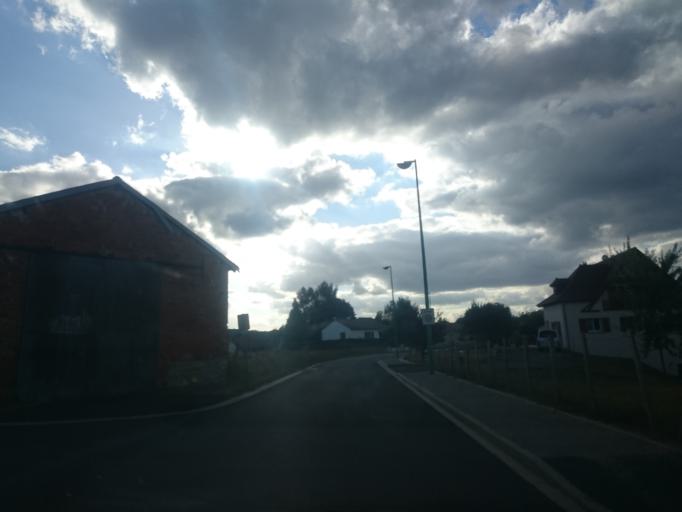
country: FR
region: Auvergne
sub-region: Departement du Cantal
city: Saint-Mamet-la-Salvetat
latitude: 44.8564
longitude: 2.2294
